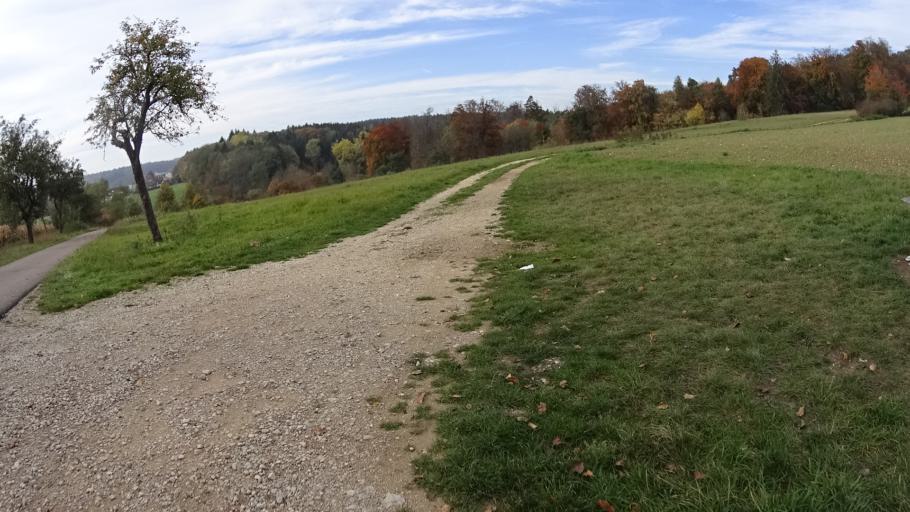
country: DE
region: Bavaria
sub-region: Upper Bavaria
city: Adelschlag
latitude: 48.8614
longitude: 11.2258
